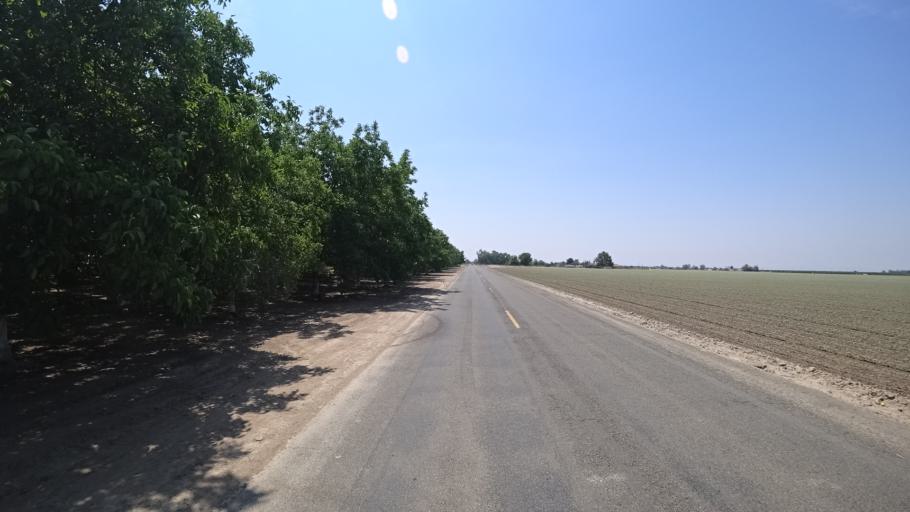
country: US
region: California
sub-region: Kings County
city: Lemoore
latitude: 36.3242
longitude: -119.7943
